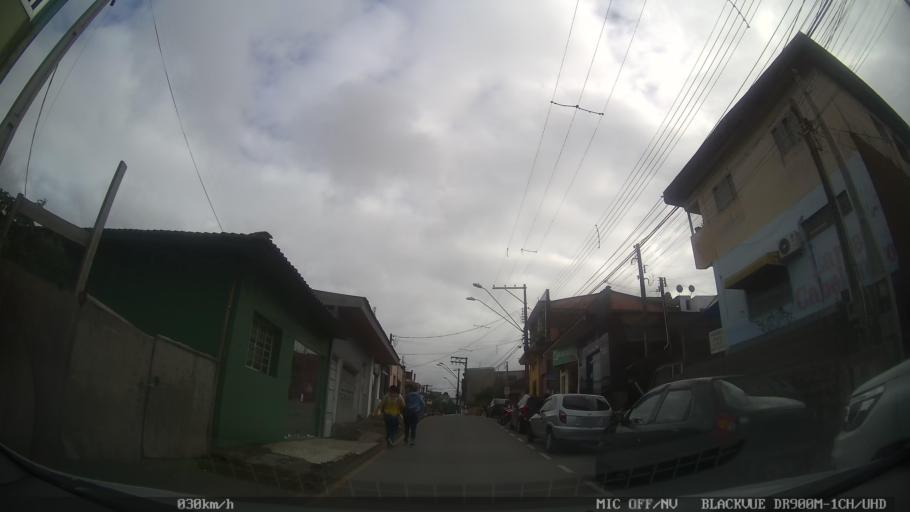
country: BR
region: Sao Paulo
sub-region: Cajati
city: Cajati
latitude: -24.7272
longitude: -48.1093
